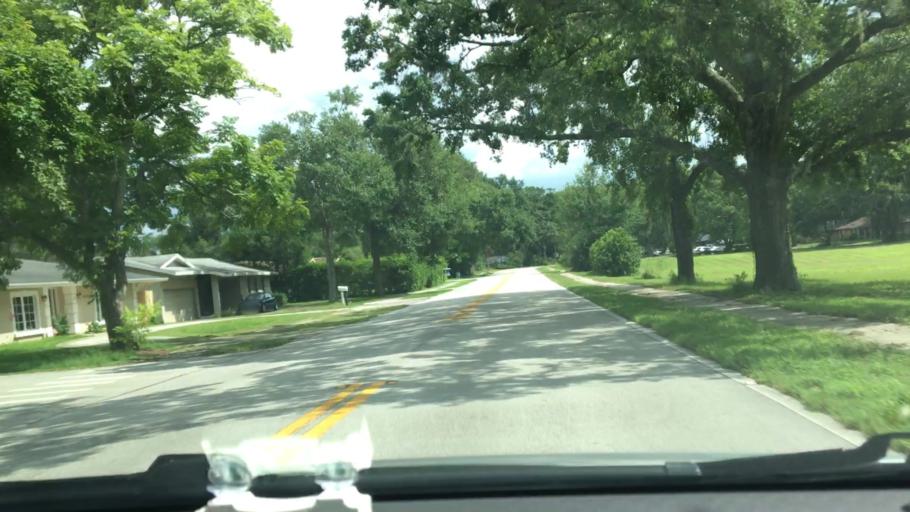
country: US
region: Florida
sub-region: Seminole County
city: Altamonte Springs
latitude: 28.6910
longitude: -81.3712
